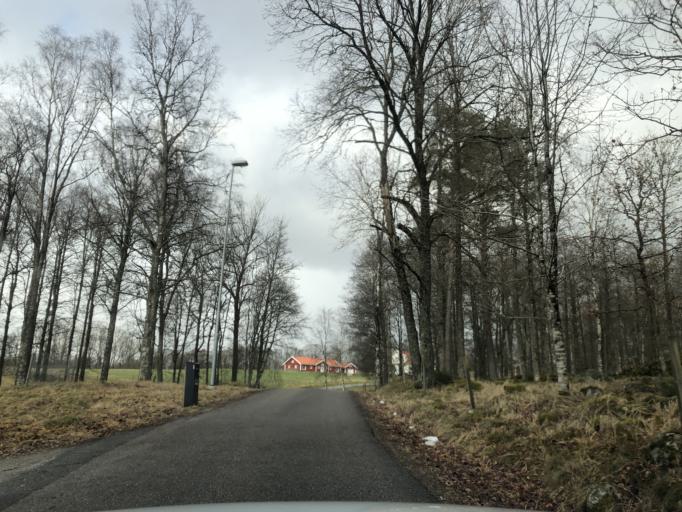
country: SE
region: Vaestra Goetaland
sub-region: Ulricehamns Kommun
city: Ulricehamn
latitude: 57.7681
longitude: 13.4168
